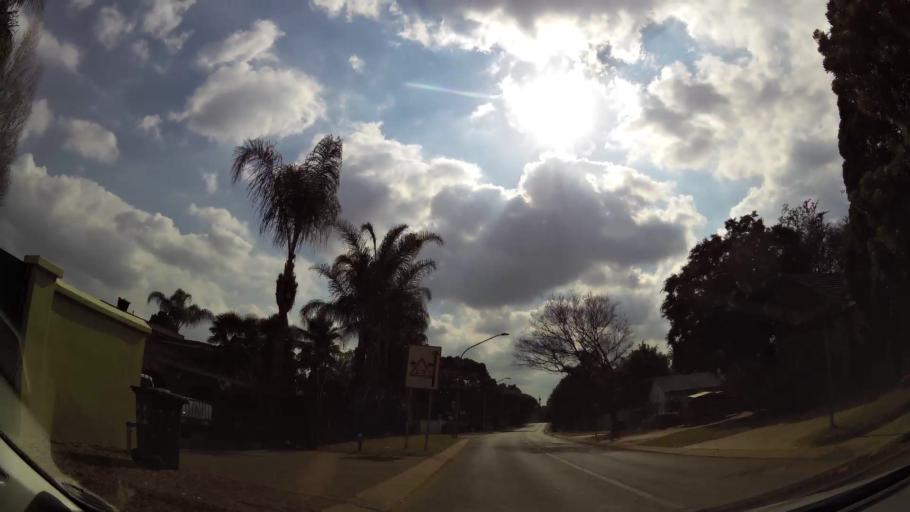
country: ZA
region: Gauteng
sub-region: City of Tshwane Metropolitan Municipality
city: Pretoria
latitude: -25.7551
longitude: 28.3132
